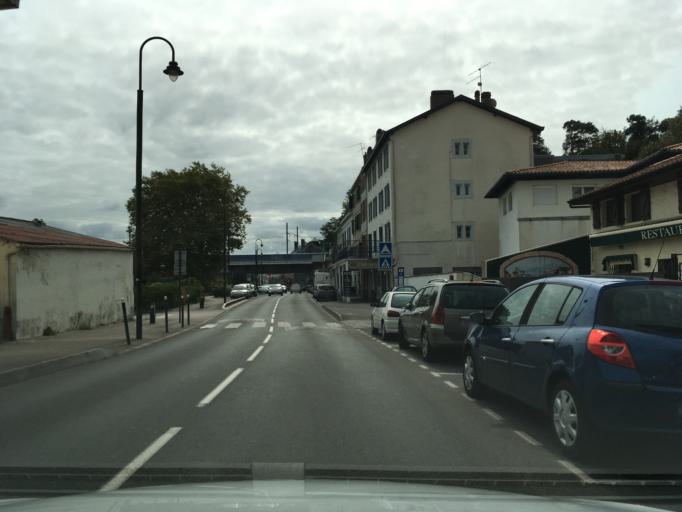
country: FR
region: Aquitaine
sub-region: Departement des Pyrenees-Atlantiques
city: Bayonne
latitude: 43.4893
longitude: -1.4666
